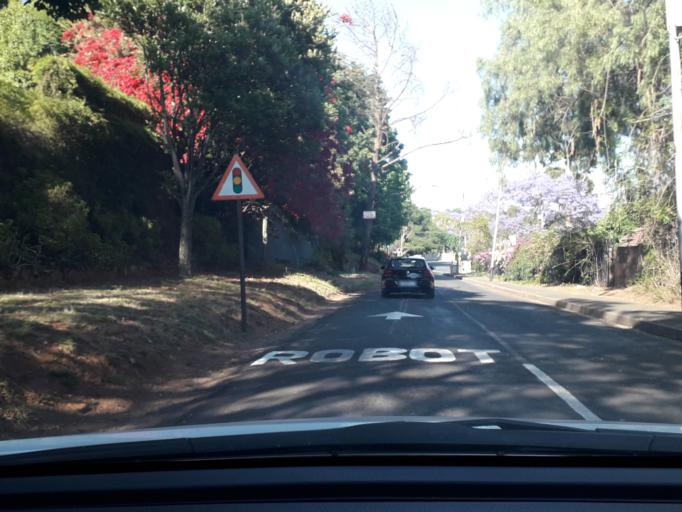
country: ZA
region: Gauteng
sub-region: City of Johannesburg Metropolitan Municipality
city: Johannesburg
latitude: -26.1712
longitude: 28.0177
